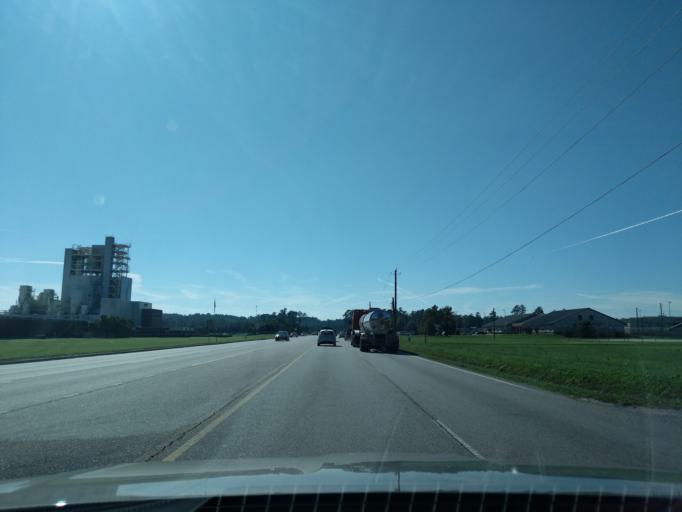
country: US
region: Georgia
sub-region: Richmond County
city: Augusta
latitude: 33.3938
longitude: -82.0053
